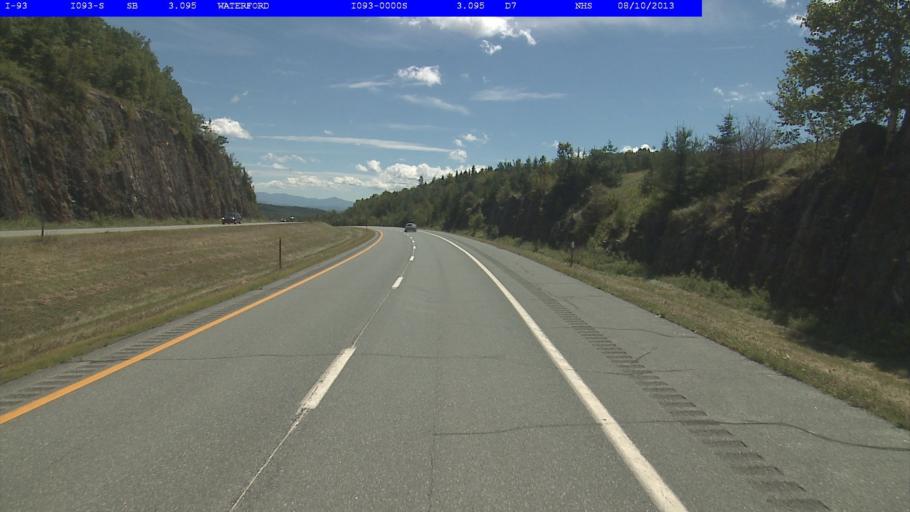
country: US
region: Vermont
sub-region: Caledonia County
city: Saint Johnsbury
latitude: 44.3809
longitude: -71.9215
